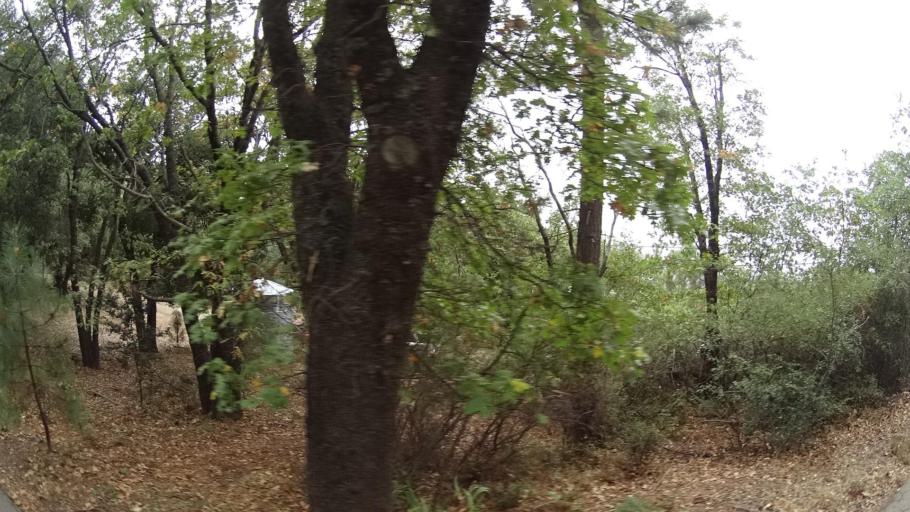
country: US
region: California
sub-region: San Diego County
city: Julian
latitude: 33.0419
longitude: -116.6272
